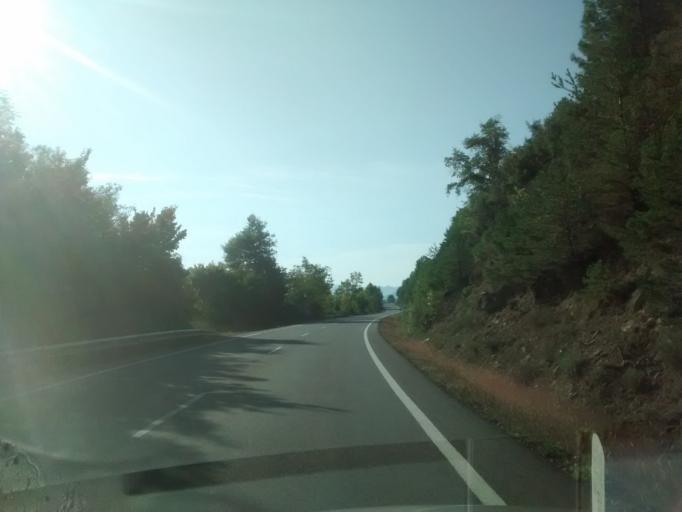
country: ES
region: Aragon
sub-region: Provincia de Huesca
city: Ainsa
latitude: 42.4266
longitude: 0.1366
